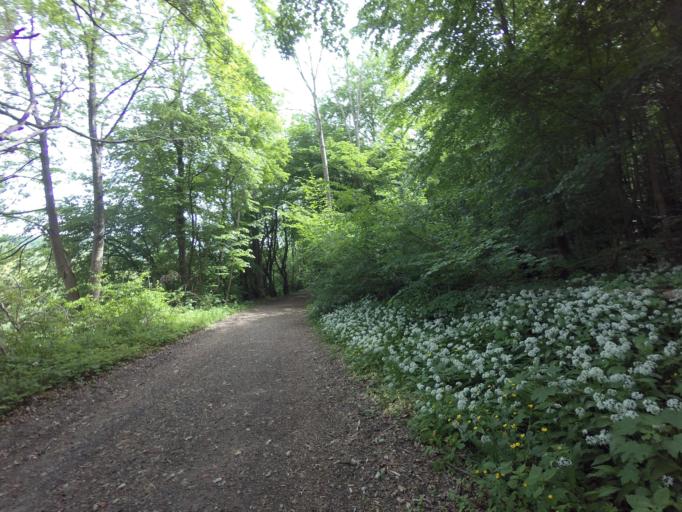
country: DE
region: Lower Saxony
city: Erkerode
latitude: 52.2063
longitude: 10.7428
